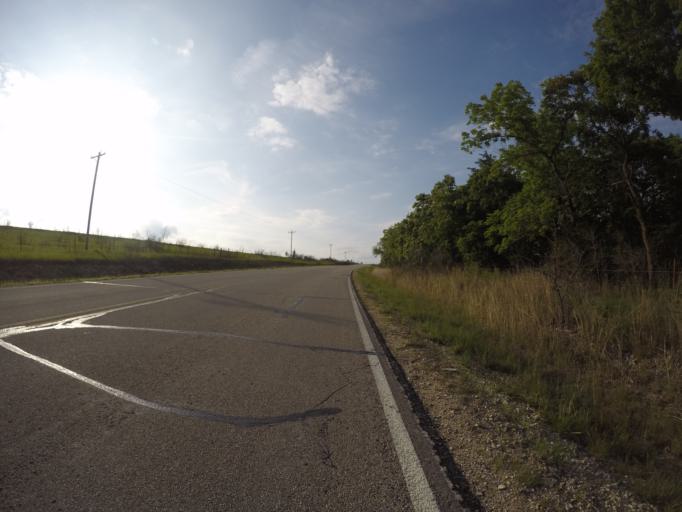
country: US
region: Kansas
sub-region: Pottawatomie County
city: Westmoreland
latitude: 39.4021
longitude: -96.6046
